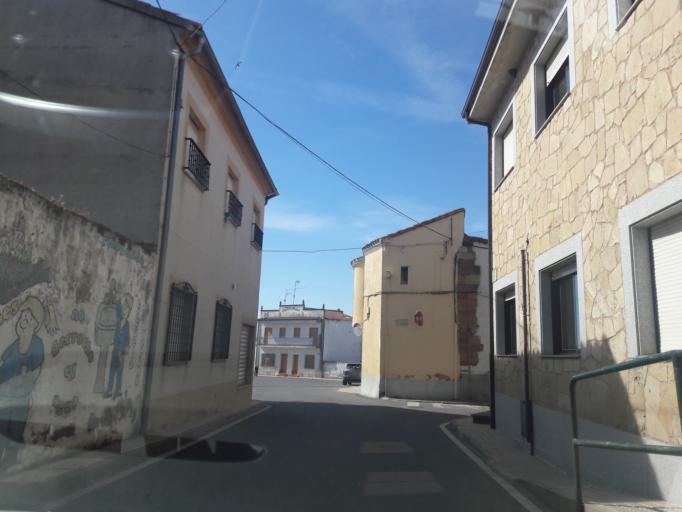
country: ES
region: Castille and Leon
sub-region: Provincia de Salamanca
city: Villoruela
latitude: 41.0086
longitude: -5.3945
